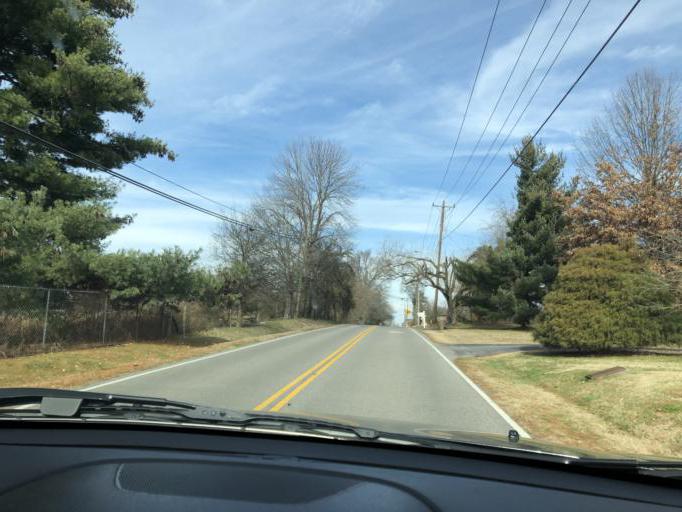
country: US
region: Tennessee
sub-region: Davidson County
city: Lakewood
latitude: 36.2214
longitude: -86.6890
